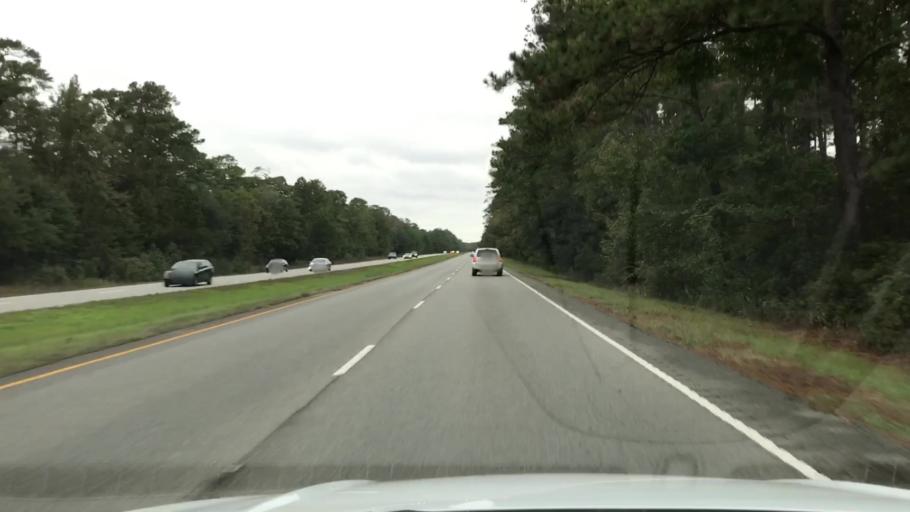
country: US
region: South Carolina
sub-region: Georgetown County
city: Georgetown
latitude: 33.3891
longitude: -79.2040
